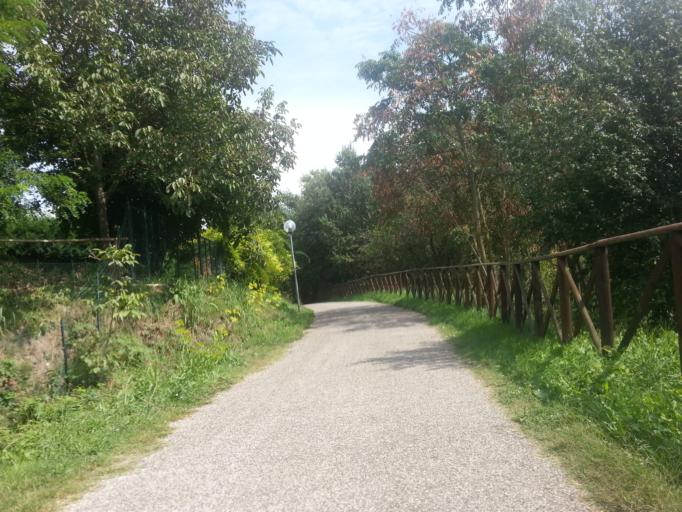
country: IT
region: Emilia-Romagna
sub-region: Provincia di Reggio Emilia
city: Reggio nell'Emilia
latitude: 44.6689
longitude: 10.6035
